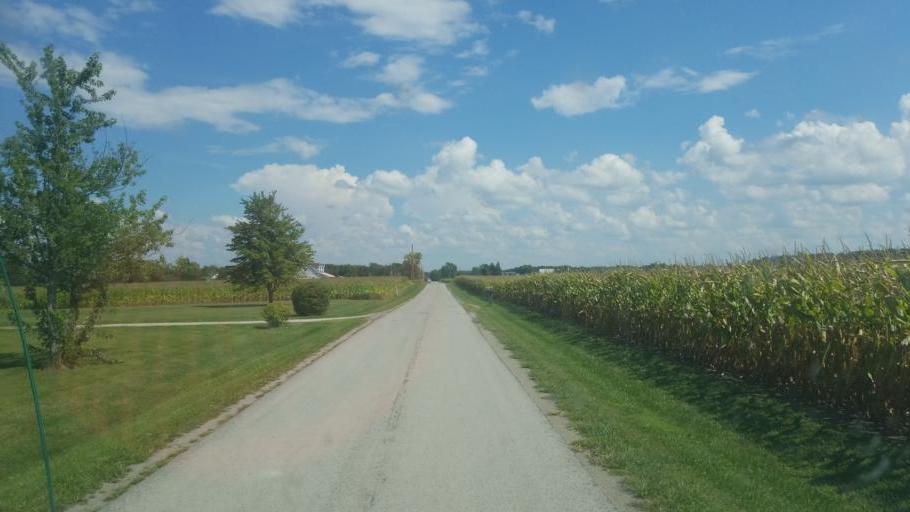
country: US
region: Ohio
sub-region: Wyandot County
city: Carey
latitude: 40.8755
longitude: -83.3968
